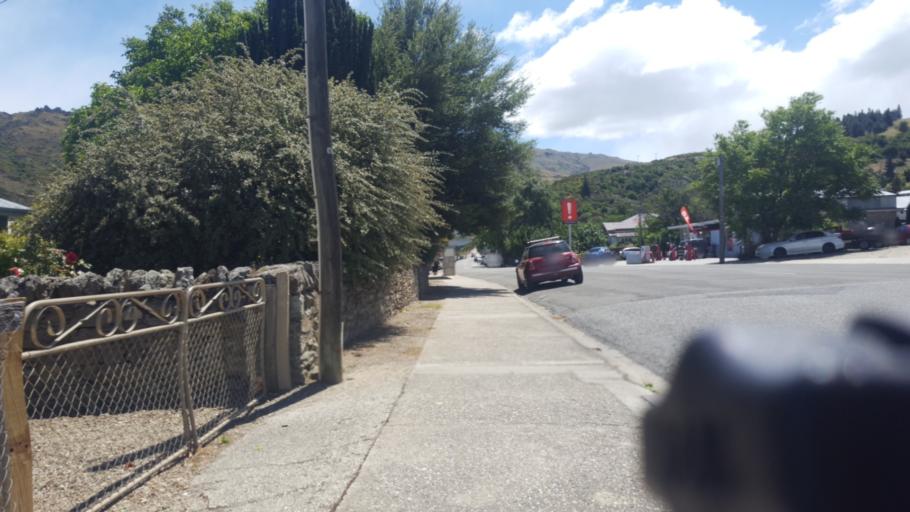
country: NZ
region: Otago
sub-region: Queenstown-Lakes District
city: Wanaka
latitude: -45.1876
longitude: 169.3174
